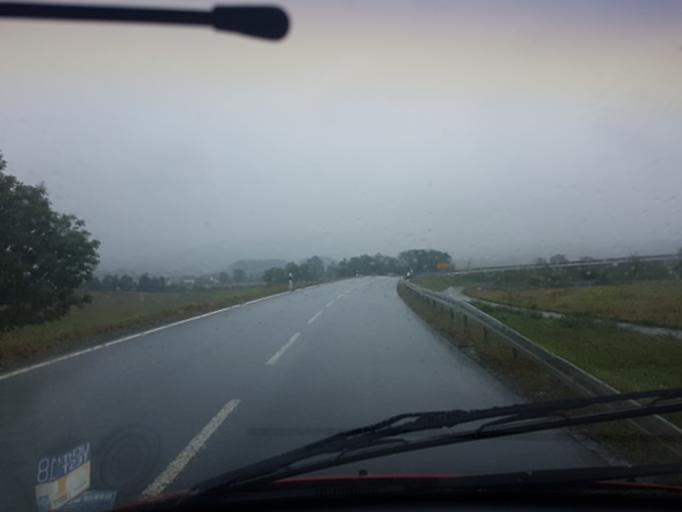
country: DE
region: Bavaria
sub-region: Upper Franconia
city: Goldkronach
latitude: 49.9893
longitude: 11.6544
